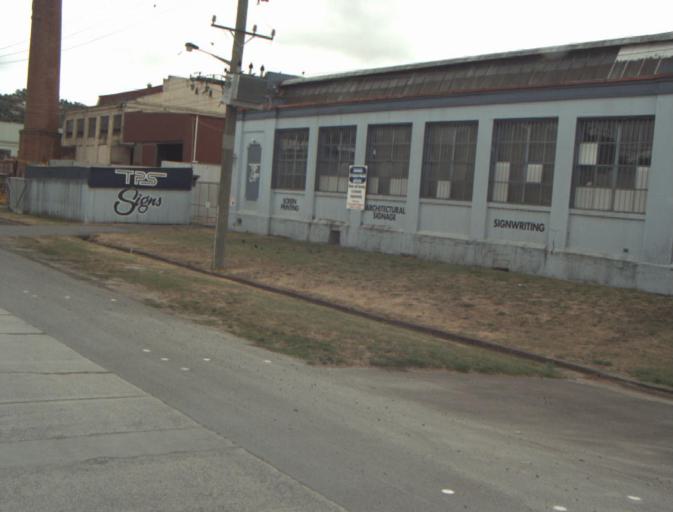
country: AU
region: Tasmania
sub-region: Launceston
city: Launceston
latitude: -41.4284
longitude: 147.1275
